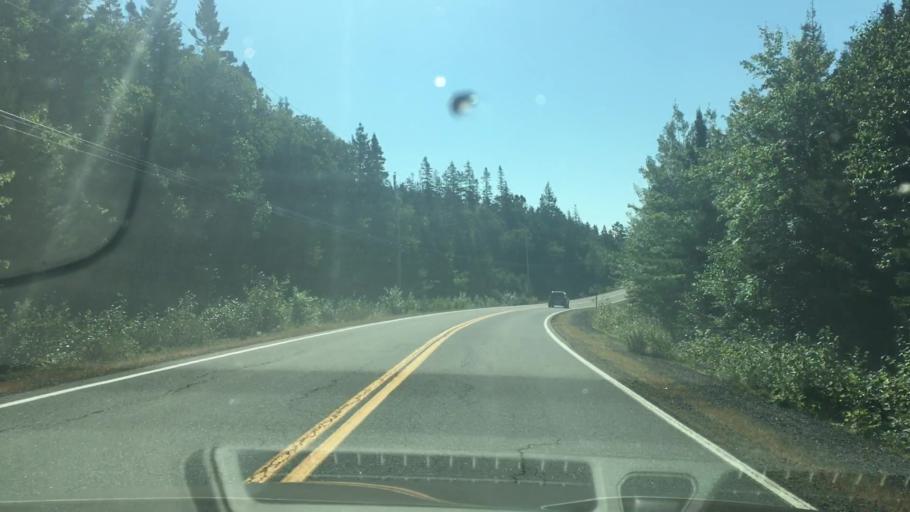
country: CA
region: Nova Scotia
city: Cole Harbour
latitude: 44.8109
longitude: -62.8361
